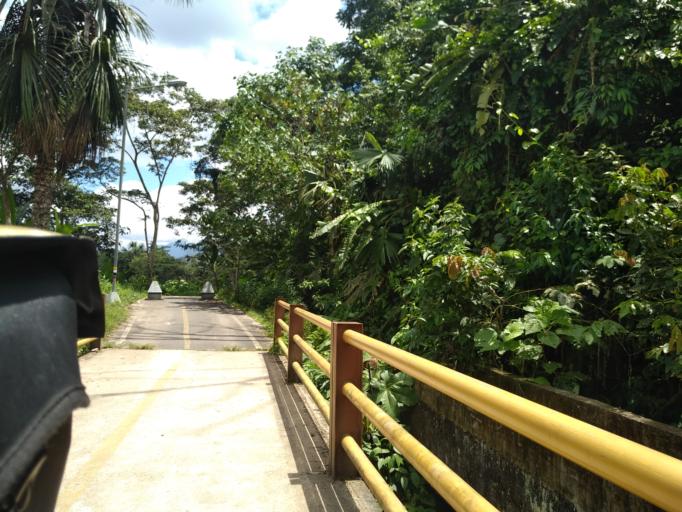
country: EC
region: Napo
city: Tena
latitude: -0.9890
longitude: -77.8232
